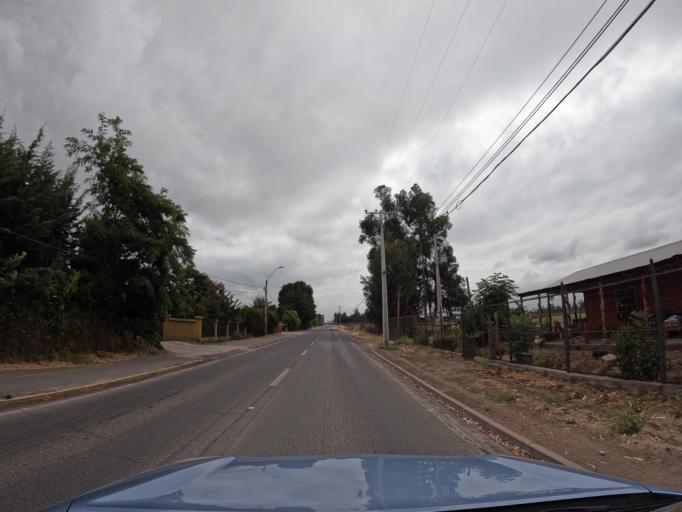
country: CL
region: O'Higgins
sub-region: Provincia de Colchagua
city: Chimbarongo
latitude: -34.7196
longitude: -71.0515
